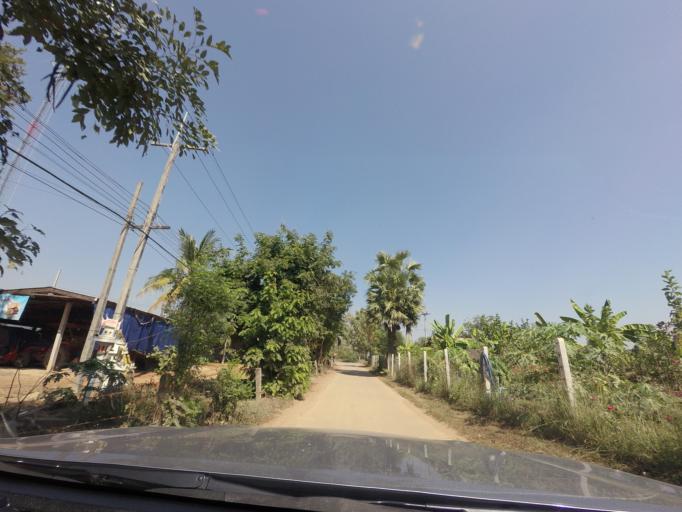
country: TH
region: Sukhothai
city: Si Samrong
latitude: 17.2011
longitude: 99.7733
